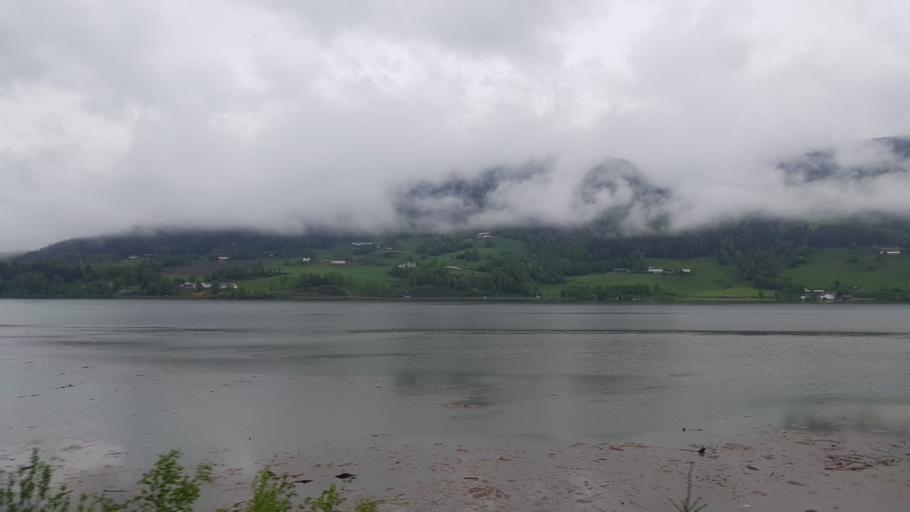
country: NO
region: Oppland
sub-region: Ringebu
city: Ringebu
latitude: 61.4298
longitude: 10.1931
